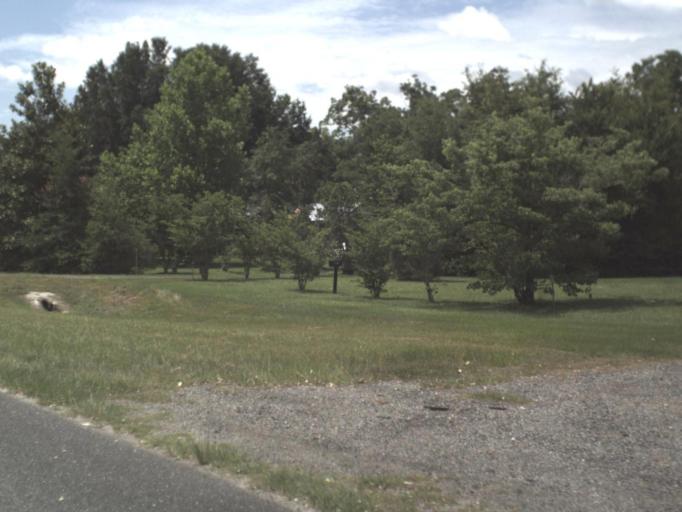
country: US
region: Florida
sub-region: Suwannee County
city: Live Oak
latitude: 30.1755
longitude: -82.9814
